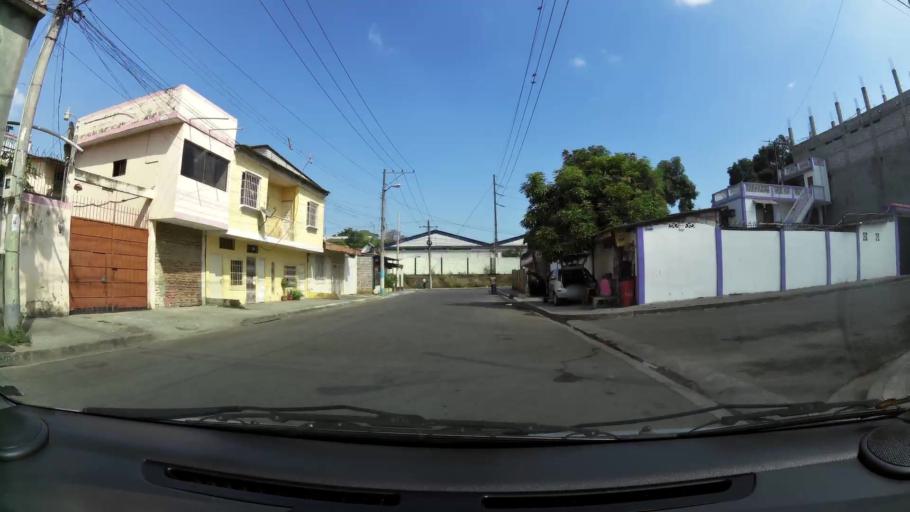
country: EC
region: Guayas
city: Guayaquil
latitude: -2.1432
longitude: -79.9394
